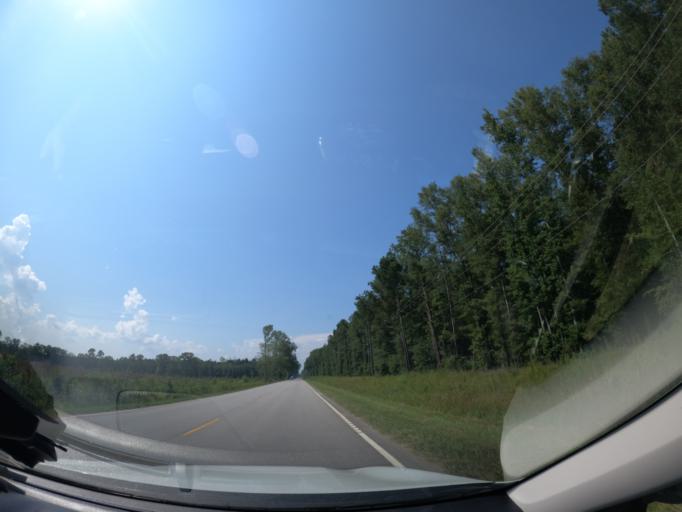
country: US
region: South Carolina
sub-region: Richland County
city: Hopkins
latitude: 33.8811
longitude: -80.9042
